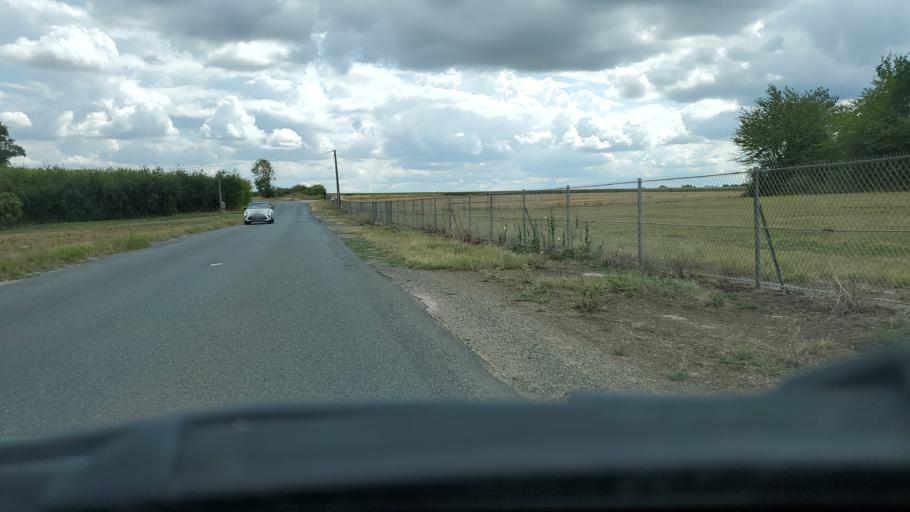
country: FR
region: Ile-de-France
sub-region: Departement de Seine-et-Marne
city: Pommeuse
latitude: 48.8449
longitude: 3.0185
